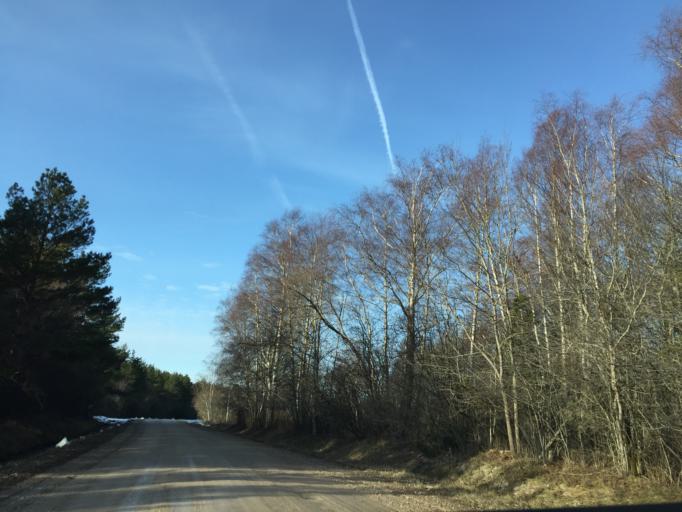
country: EE
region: Saare
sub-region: Kuressaare linn
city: Kuressaare
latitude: 58.3674
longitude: 22.0280
